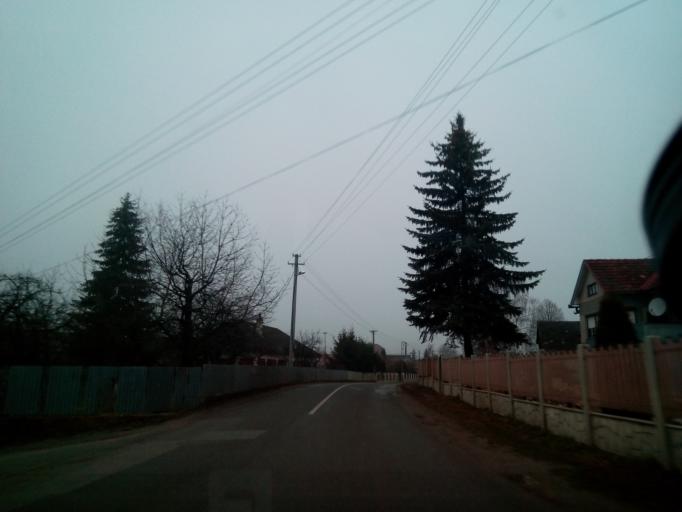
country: SK
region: Kosicky
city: Krompachy
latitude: 48.9729
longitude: 20.9513
